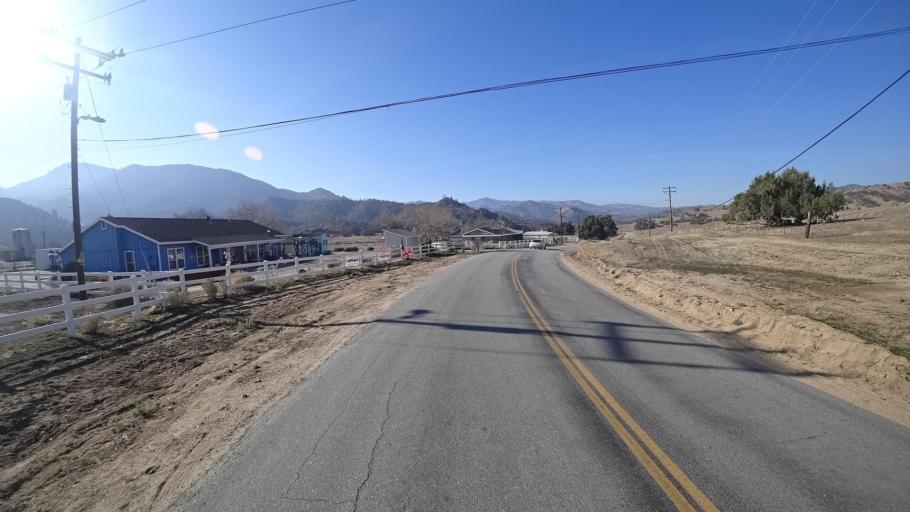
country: US
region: California
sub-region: Kern County
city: Tehachapi
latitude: 35.3187
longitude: -118.3929
